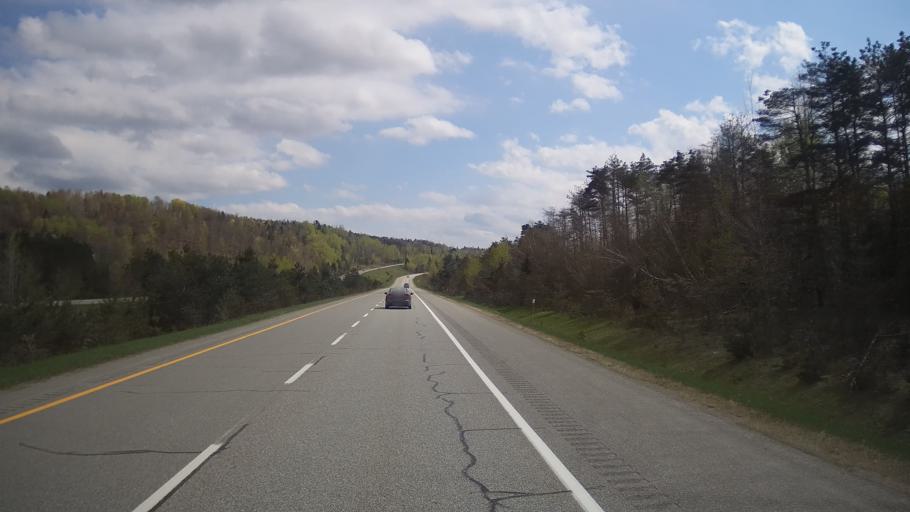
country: CA
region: Quebec
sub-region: Estrie
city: Magog
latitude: 45.1142
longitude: -72.0717
